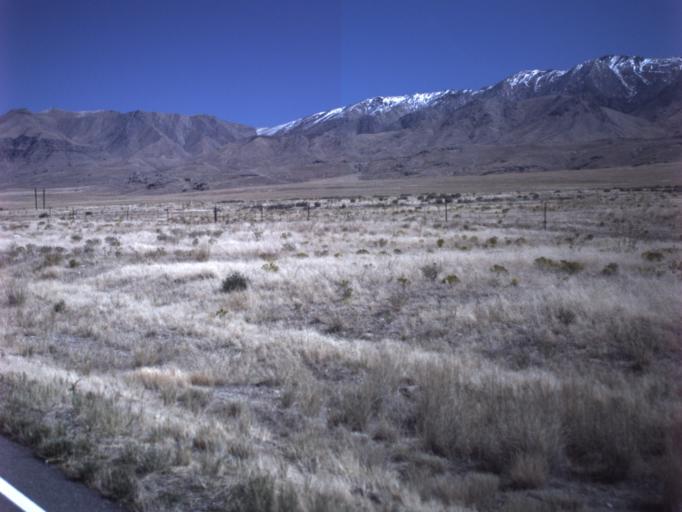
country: US
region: Utah
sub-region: Tooele County
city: Grantsville
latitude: 40.5933
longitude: -112.7188
